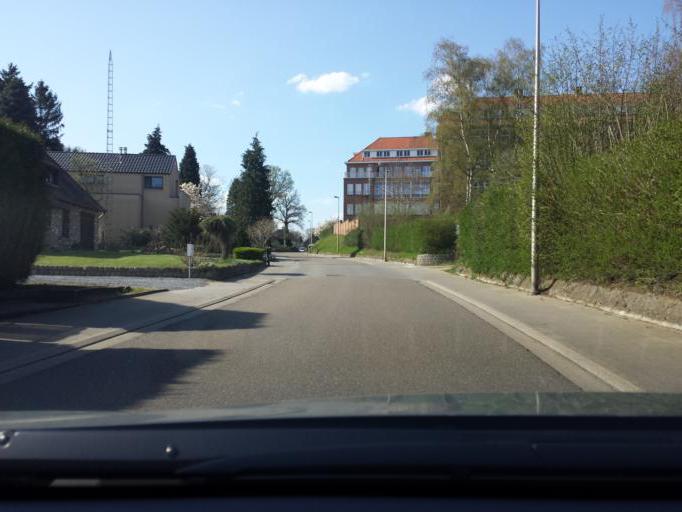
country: BE
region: Flanders
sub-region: Provincie Limburg
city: Halen
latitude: 50.9755
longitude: 5.1093
